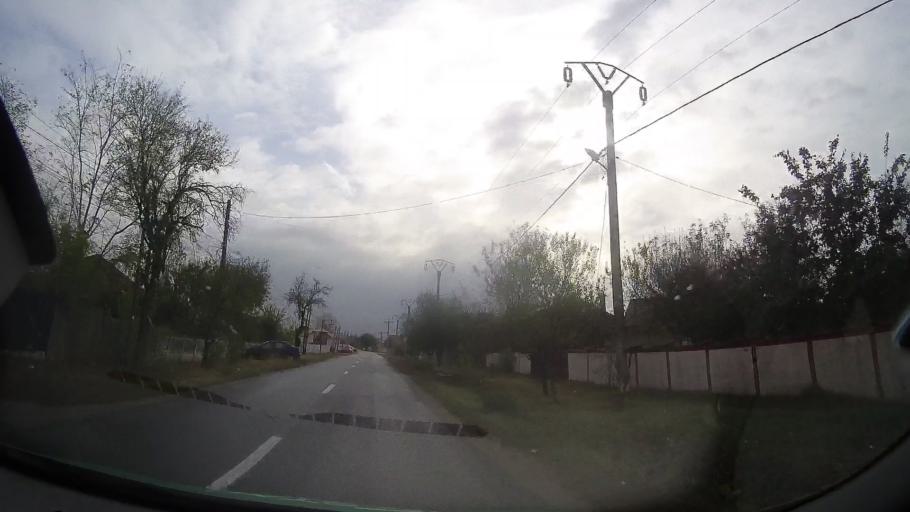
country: RO
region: Ialomita
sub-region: Comuna Fierbinti-Targ
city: Fierbintii de Jos
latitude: 44.6974
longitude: 26.3940
